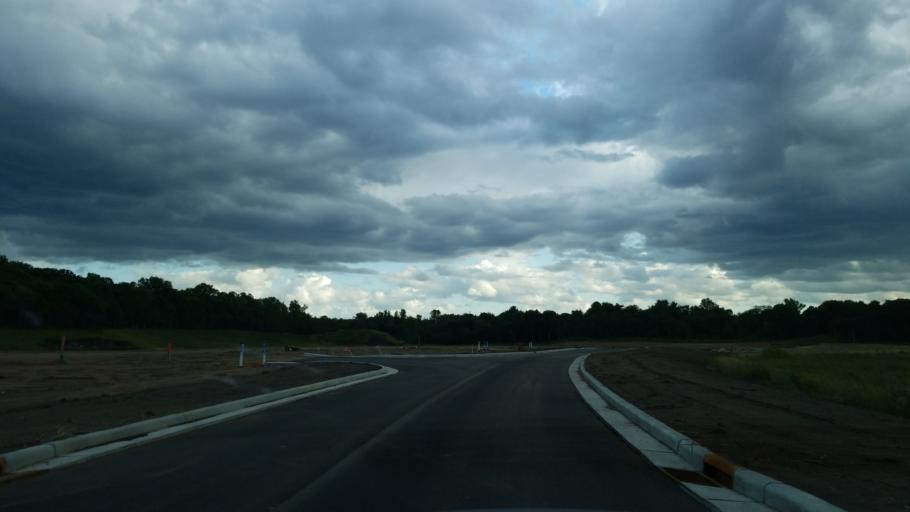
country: US
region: Minnesota
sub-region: Washington County
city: Lakeland
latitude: 44.9470
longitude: -92.7254
